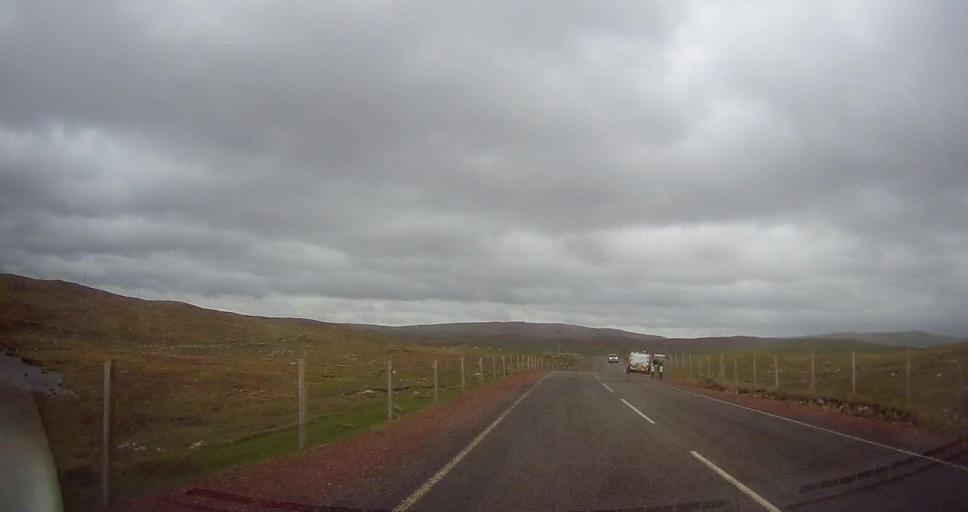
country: GB
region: Scotland
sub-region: Shetland Islands
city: Lerwick
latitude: 60.4795
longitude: -1.4413
